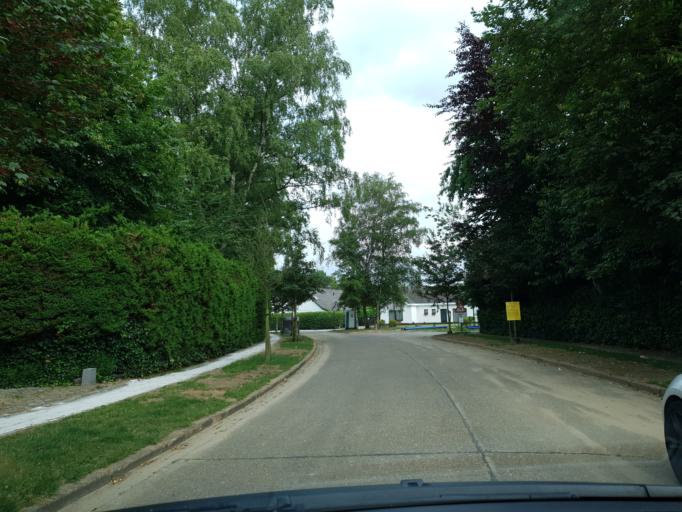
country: BE
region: Flanders
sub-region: Provincie Antwerpen
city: Brasschaat
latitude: 51.2718
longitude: 4.4551
